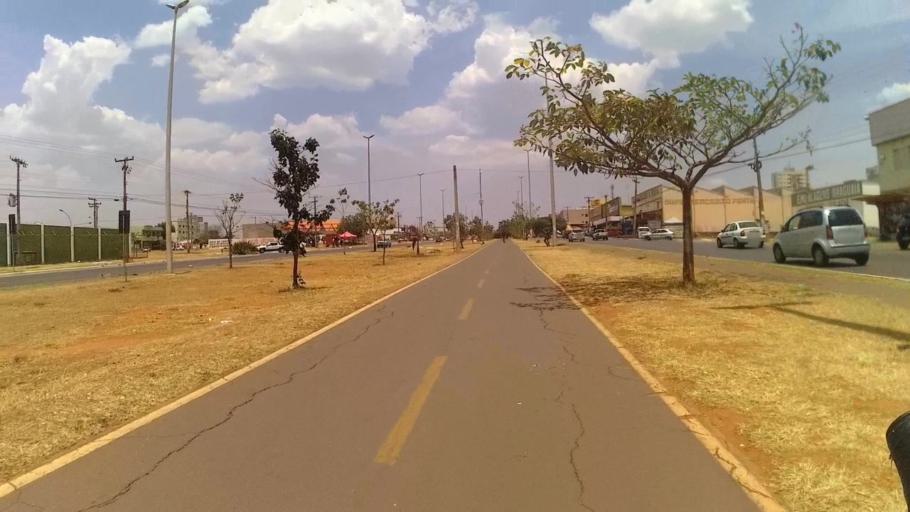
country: BR
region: Federal District
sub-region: Brasilia
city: Brasilia
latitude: -15.8746
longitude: -48.0761
